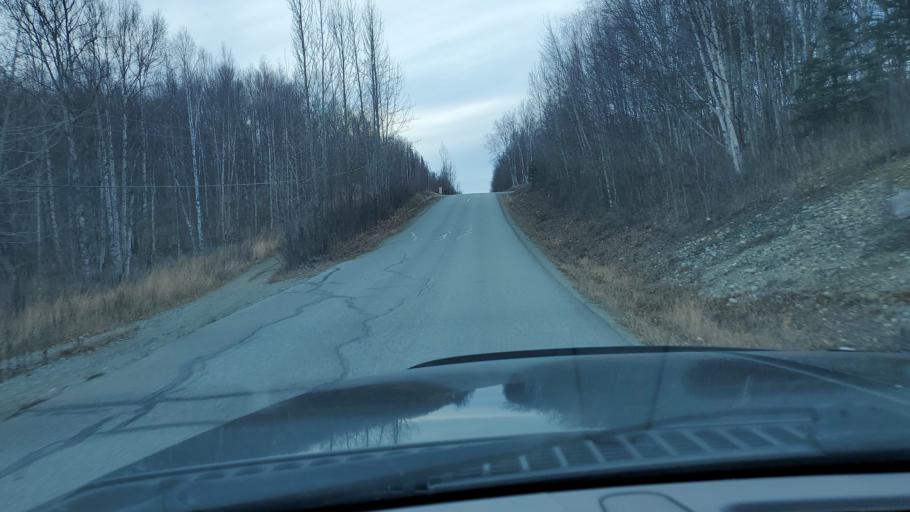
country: US
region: Alaska
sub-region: Matanuska-Susitna Borough
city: Lakes
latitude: 61.6572
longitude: -149.2922
